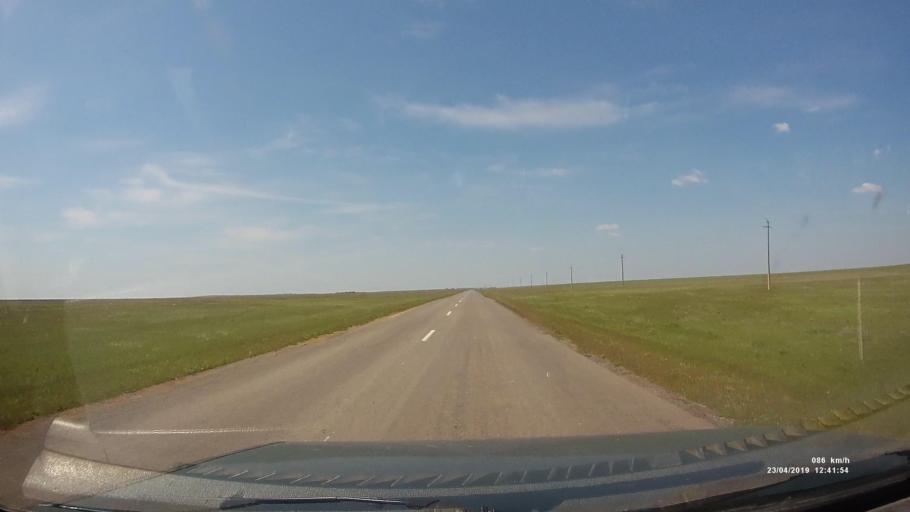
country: RU
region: Kalmykiya
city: Yashalta
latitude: 46.4517
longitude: 42.6740
